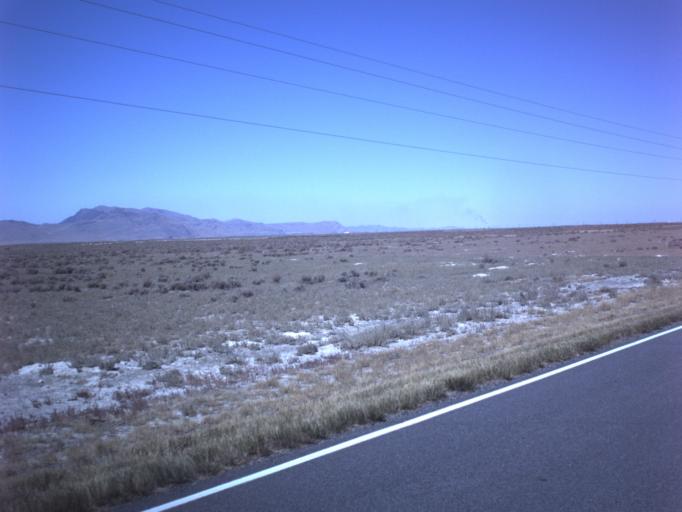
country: US
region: Utah
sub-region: Tooele County
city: Grantsville
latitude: 40.7211
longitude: -112.6601
